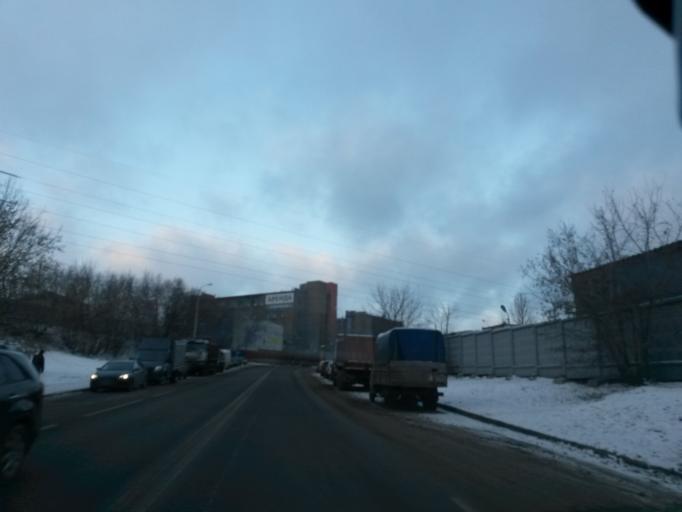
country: RU
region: Moscow
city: Amin'yevo
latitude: 55.7038
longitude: 37.4507
